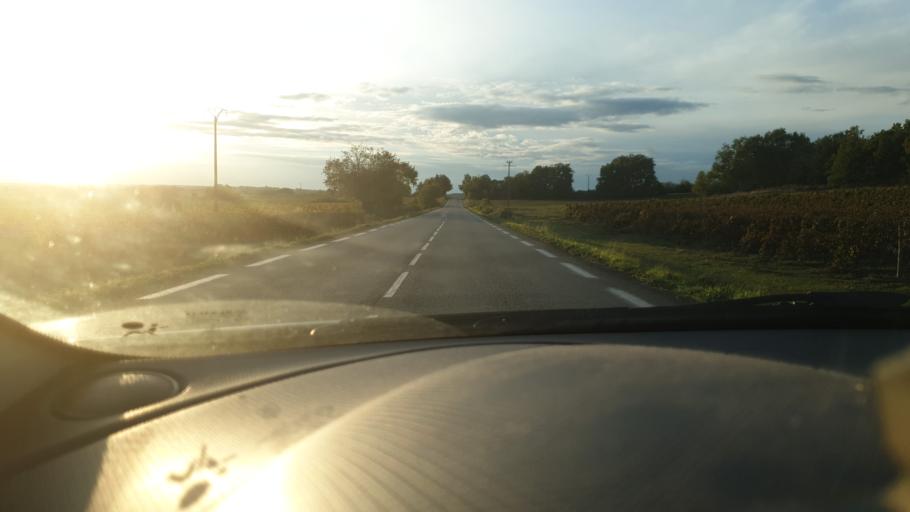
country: FR
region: Midi-Pyrenees
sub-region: Departement du Lot
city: Montcuq
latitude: 44.3998
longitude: 1.2277
